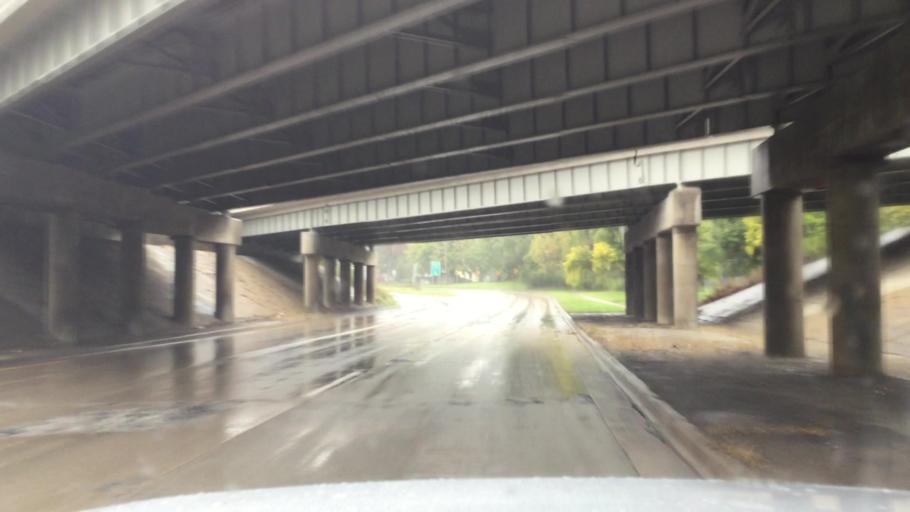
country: US
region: Michigan
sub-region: Saginaw County
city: Saginaw
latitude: 43.4403
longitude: -83.9495
